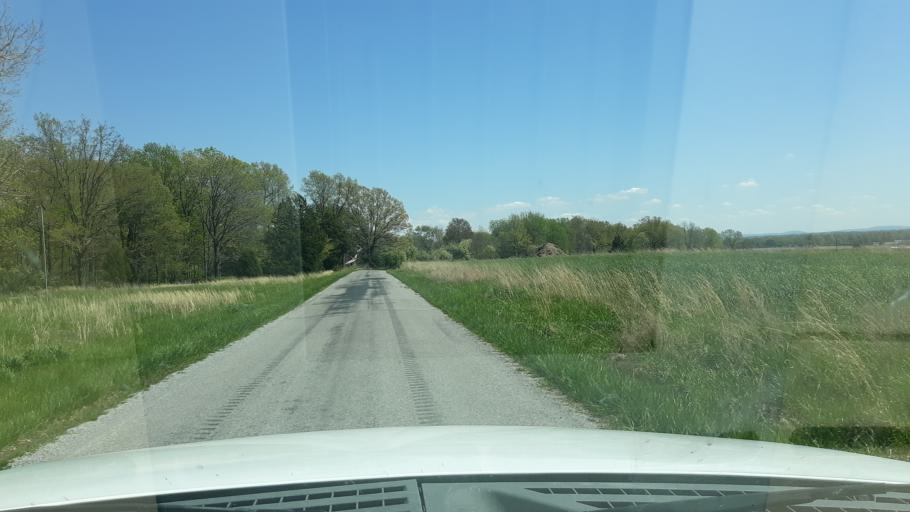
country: US
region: Illinois
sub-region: Saline County
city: Harrisburg
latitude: 37.8562
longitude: -88.6361
